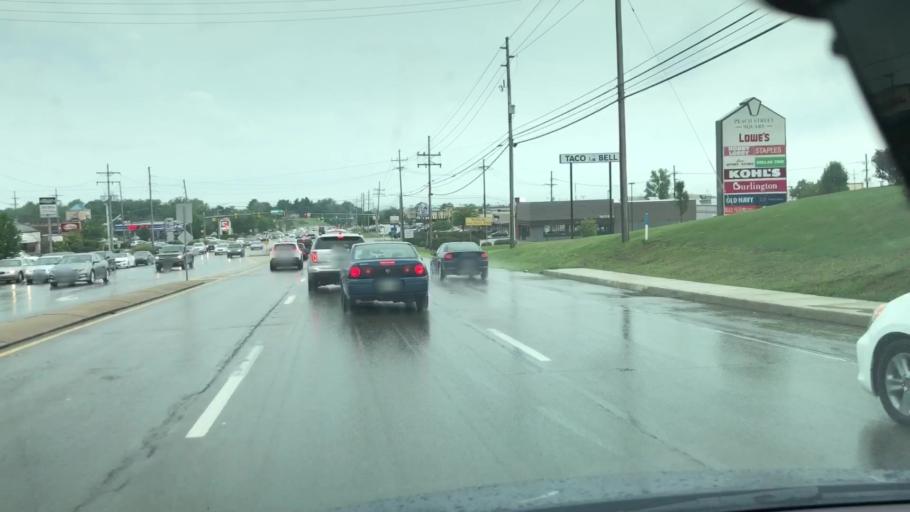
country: US
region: Pennsylvania
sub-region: Erie County
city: Erie
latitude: 42.0545
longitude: -80.0870
